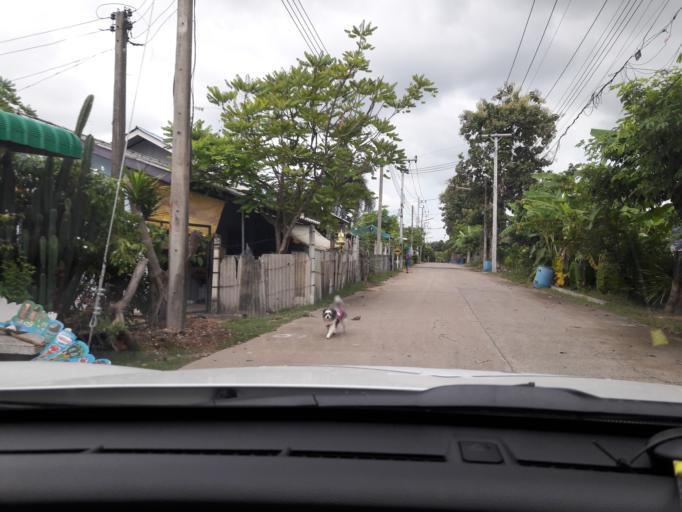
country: TH
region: Nakhon Sawan
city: Tak Fa
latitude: 15.3530
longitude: 100.4942
